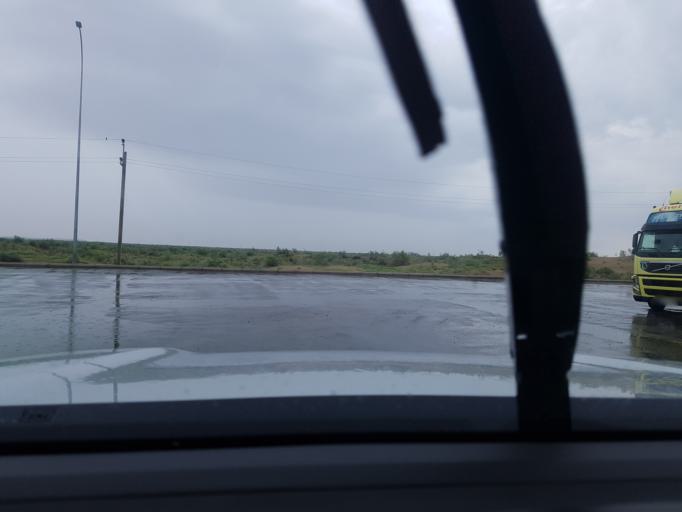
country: TM
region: Lebap
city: Farap
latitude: 39.2053
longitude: 63.6982
